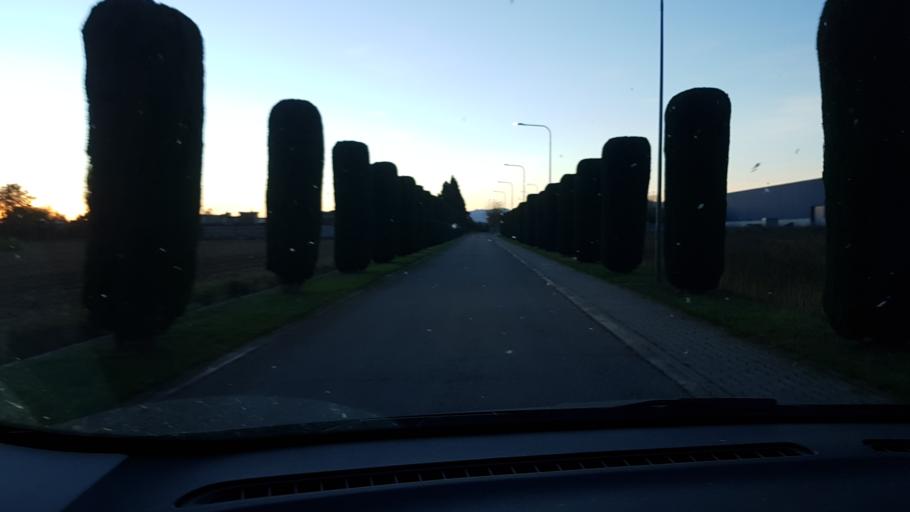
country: IT
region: Piedmont
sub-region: Provincia di Cuneo
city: Villafalletto
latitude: 44.5480
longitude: 7.5439
